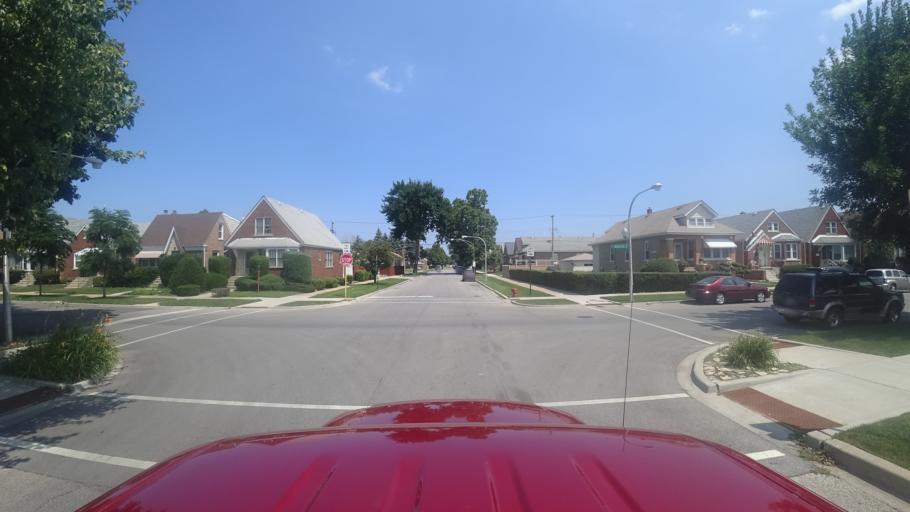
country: US
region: Illinois
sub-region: Cook County
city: Hometown
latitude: 41.7913
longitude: -87.7282
